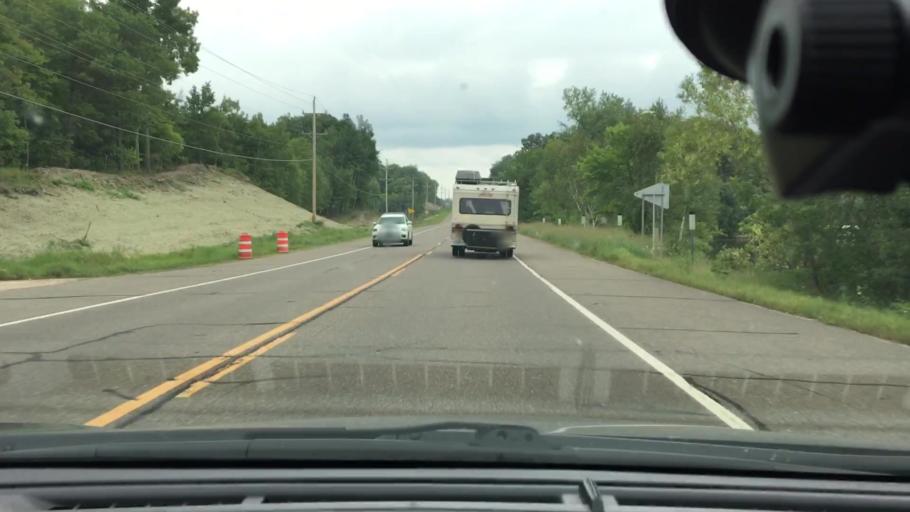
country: US
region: Minnesota
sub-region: Crow Wing County
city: Crosby
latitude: 46.4888
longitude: -93.9083
